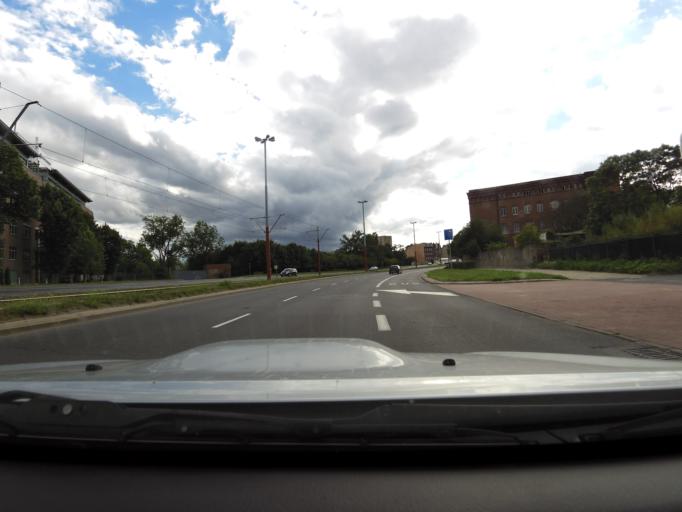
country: PL
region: Pomeranian Voivodeship
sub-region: Gdansk
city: Gdansk
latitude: 54.3457
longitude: 18.6679
